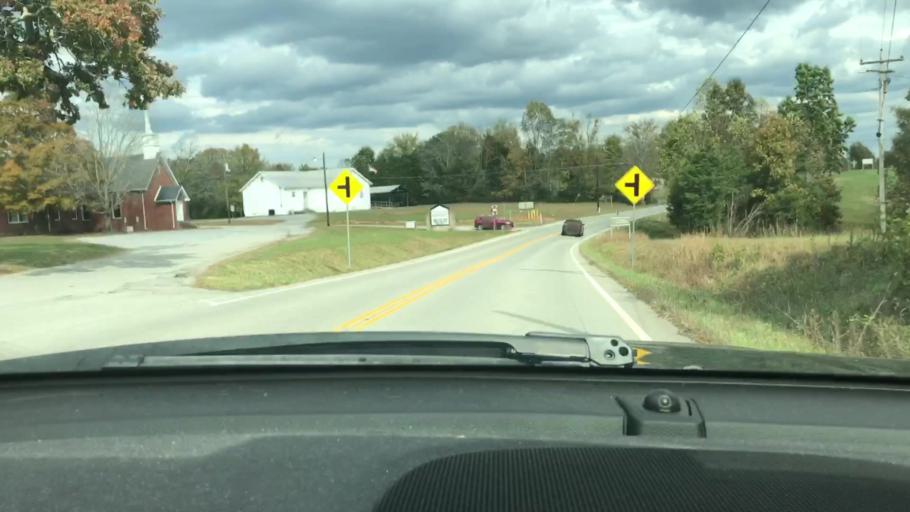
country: US
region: Tennessee
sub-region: Dickson County
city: Charlotte
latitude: 36.2547
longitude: -87.2315
